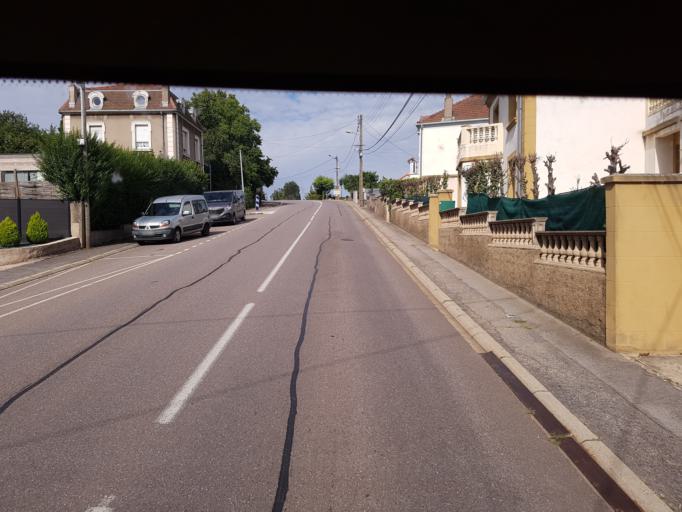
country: FR
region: Lorraine
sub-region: Departement de la Moselle
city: Sierck-les-Bains
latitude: 49.4421
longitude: 6.3494
